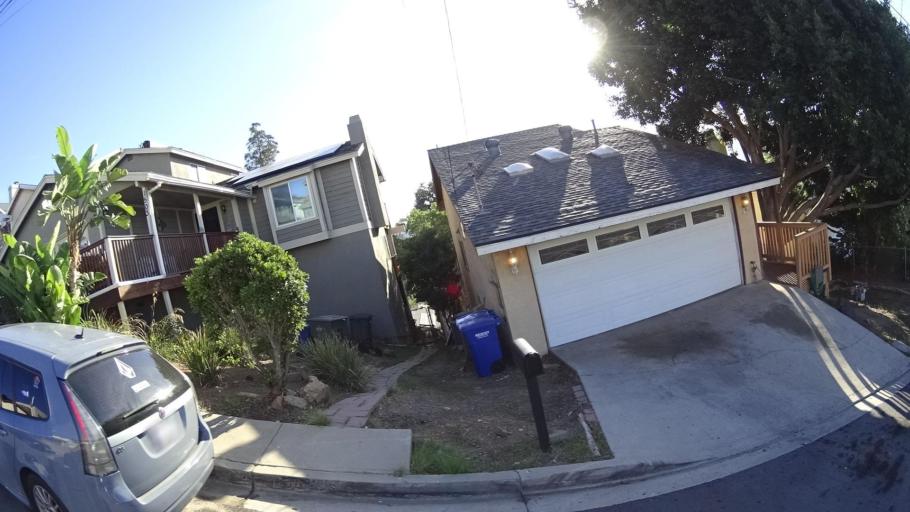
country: US
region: California
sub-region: San Diego County
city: La Presa
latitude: 32.7192
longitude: -116.9863
